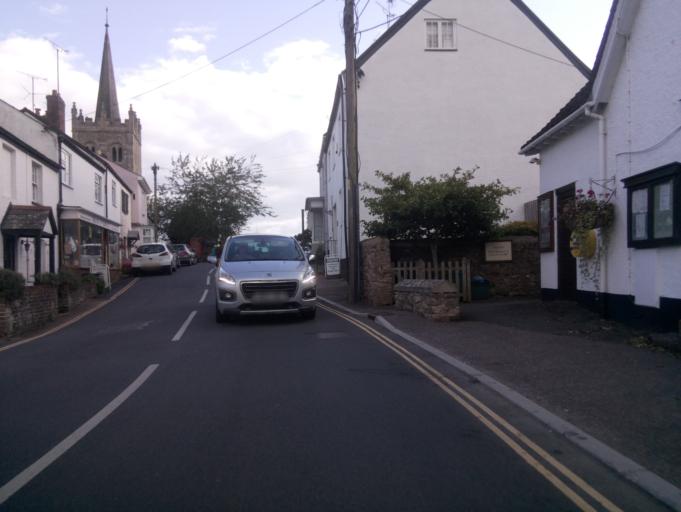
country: GB
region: England
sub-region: Devon
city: Sidmouth
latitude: 50.7195
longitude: -3.2204
